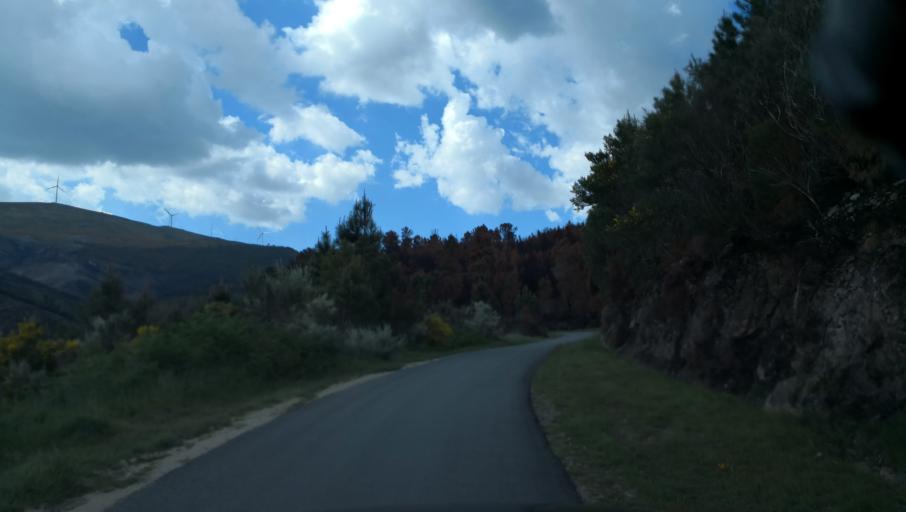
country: PT
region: Vila Real
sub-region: Vila Real
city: Vila Real
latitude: 41.3532
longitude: -7.7351
